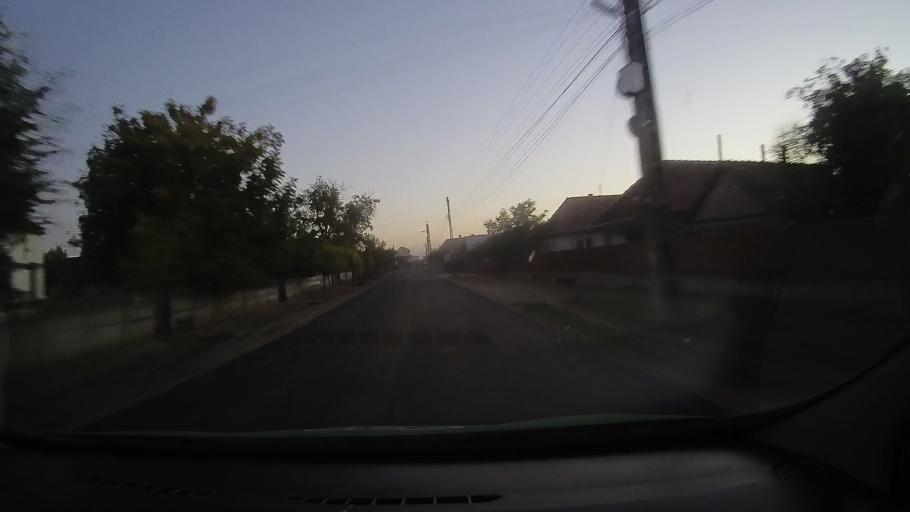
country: RO
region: Bihor
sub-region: Comuna Simian
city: Simian
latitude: 47.5029
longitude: 22.0921
